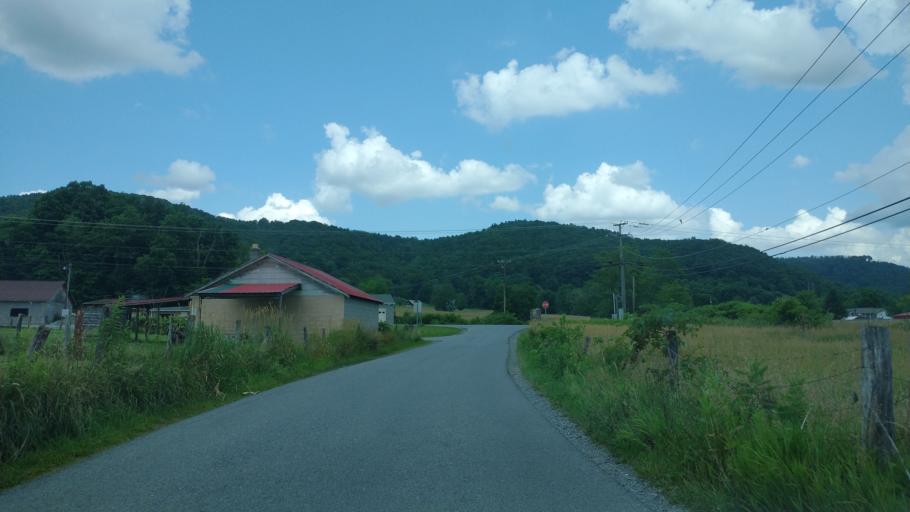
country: US
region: West Virginia
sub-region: Mercer County
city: Athens
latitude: 37.4564
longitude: -81.0111
